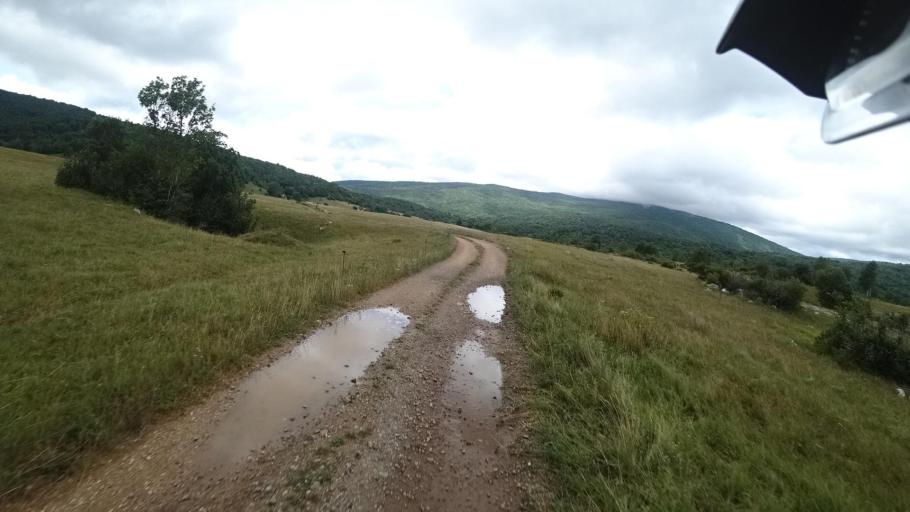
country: HR
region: Licko-Senjska
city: Jezerce
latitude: 44.7798
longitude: 15.4944
